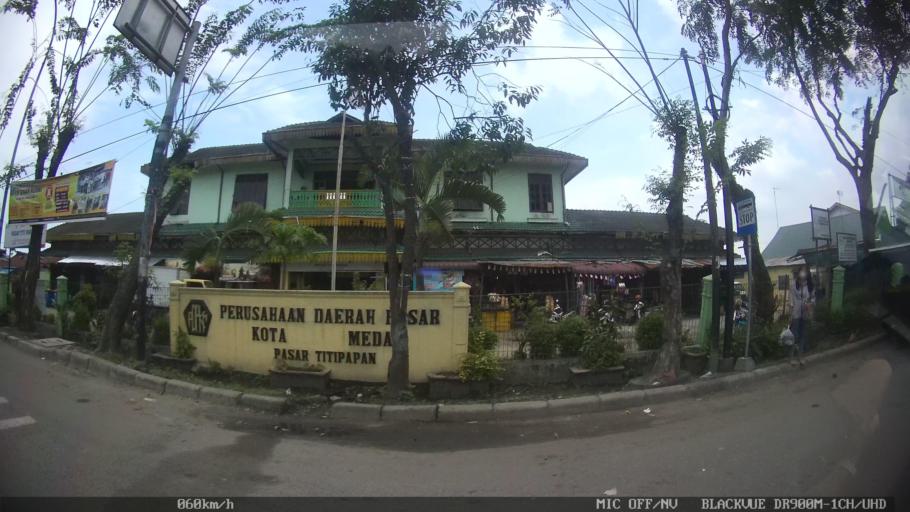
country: ID
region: North Sumatra
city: Labuhan Deli
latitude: 3.6890
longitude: 98.6685
